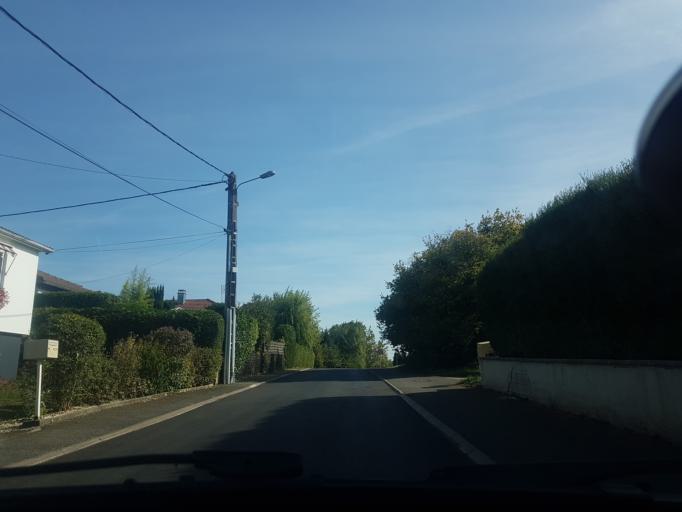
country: FR
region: Franche-Comte
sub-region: Territoire de Belfort
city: Chevremont
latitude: 47.6575
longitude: 6.9187
